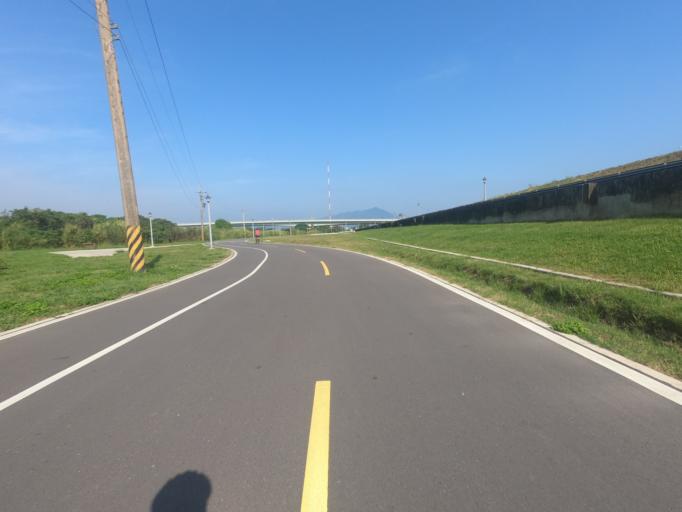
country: TW
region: Taipei
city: Taipei
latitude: 25.0979
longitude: 121.5024
